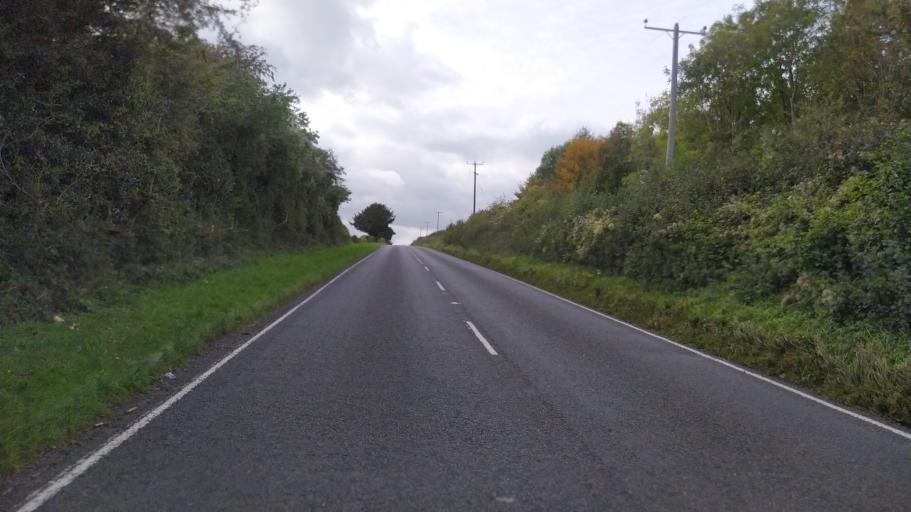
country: GB
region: England
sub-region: Hampshire
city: Andover
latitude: 51.1255
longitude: -1.4309
